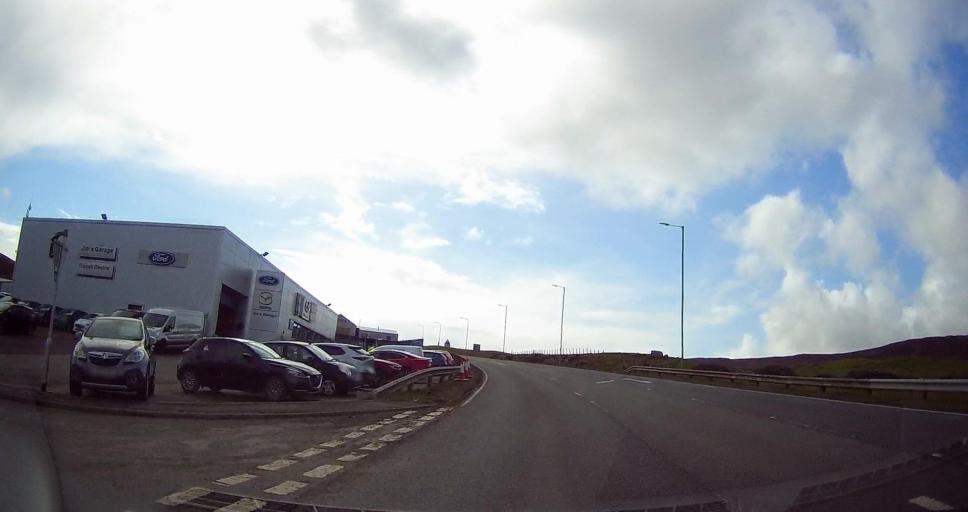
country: GB
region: Scotland
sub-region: Shetland Islands
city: Lerwick
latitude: 60.1703
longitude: -1.1700
